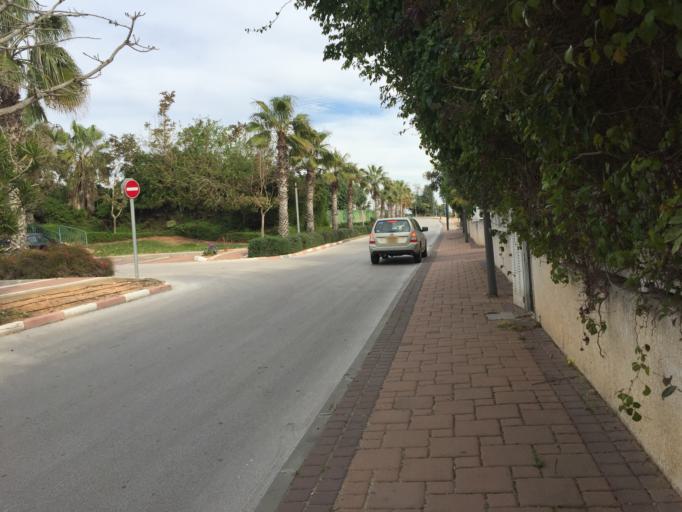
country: IL
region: Haifa
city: Qesarya
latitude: 32.5120
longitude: 34.9035
